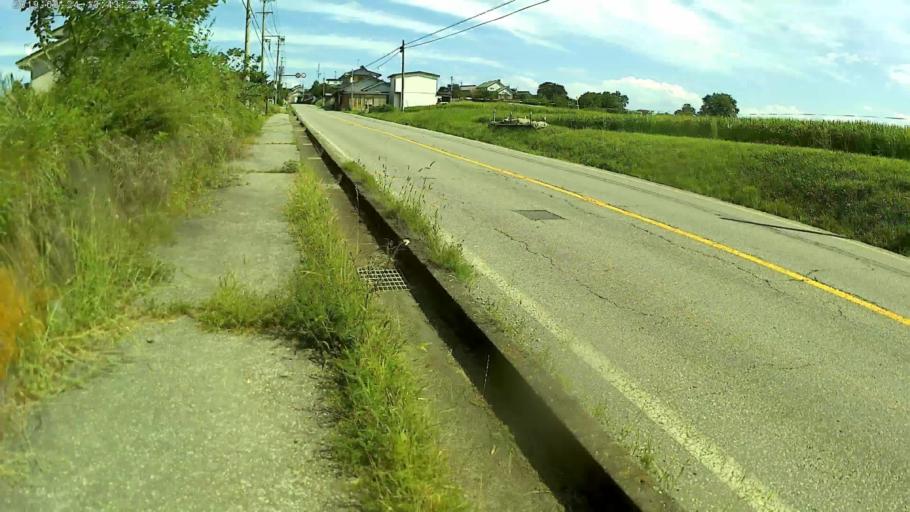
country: JP
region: Nagano
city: Komoro
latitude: 36.2754
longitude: 138.4015
